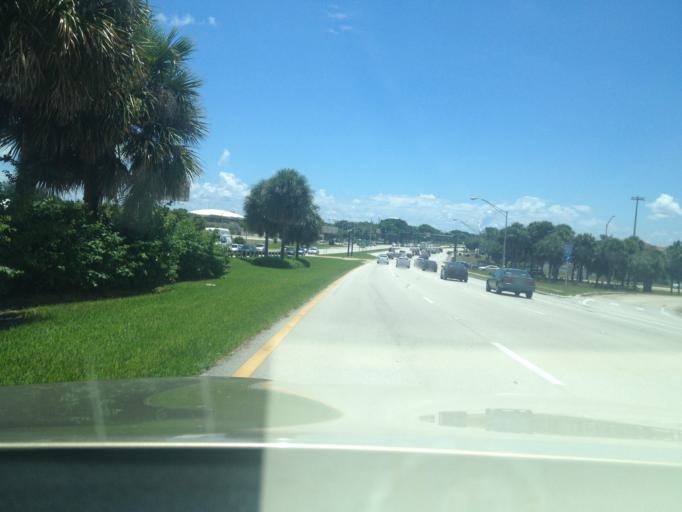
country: US
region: Florida
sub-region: Palm Beach County
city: Boca Raton
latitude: 26.3682
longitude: -80.1179
